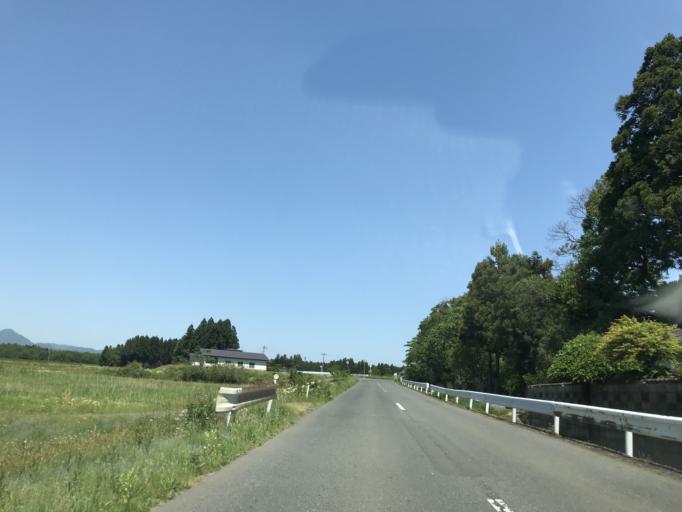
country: JP
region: Iwate
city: Mizusawa
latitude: 39.1888
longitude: 141.0764
